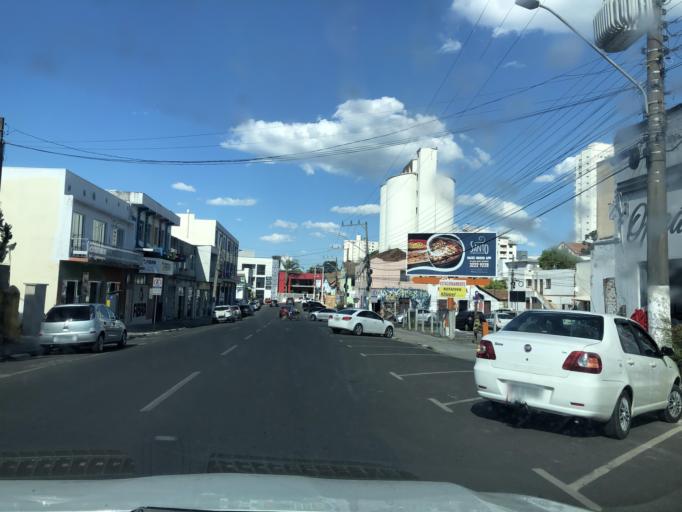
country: BR
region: Santa Catarina
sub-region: Lages
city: Lages
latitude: -27.8119
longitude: -50.3277
